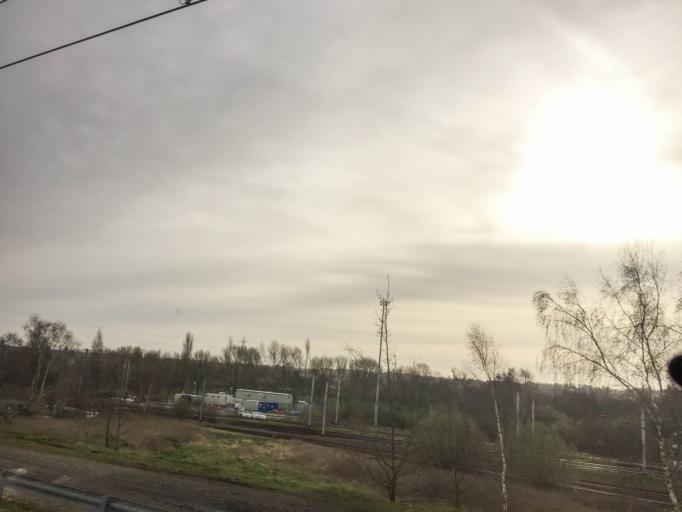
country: GB
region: England
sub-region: Warrington
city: Stockton Heath
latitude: 53.3725
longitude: -2.6082
